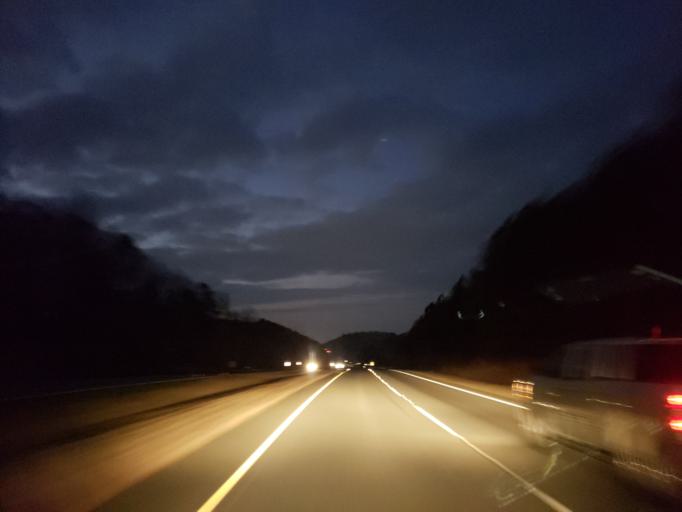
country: US
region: Georgia
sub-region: Polk County
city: Rockmart
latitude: 33.9699
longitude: -84.9997
